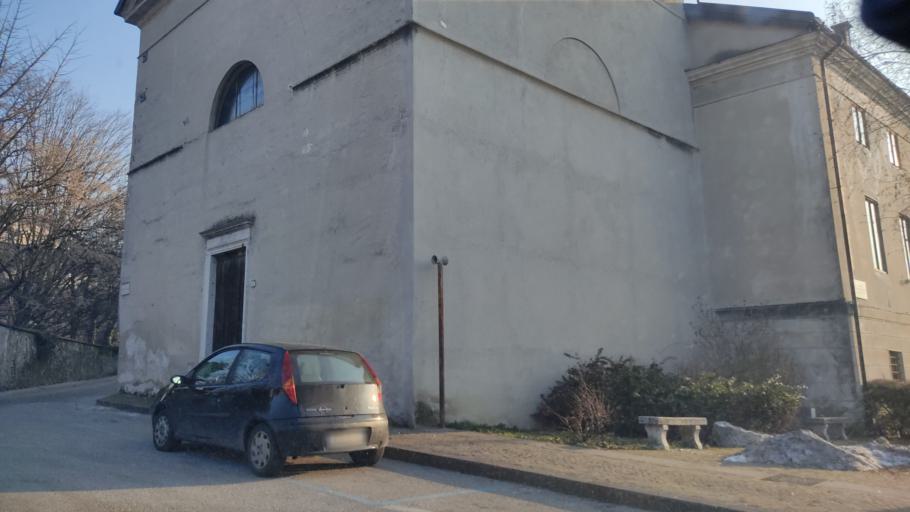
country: IT
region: Veneto
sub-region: Provincia di Belluno
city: Feltre
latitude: 46.0155
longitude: 11.9086
